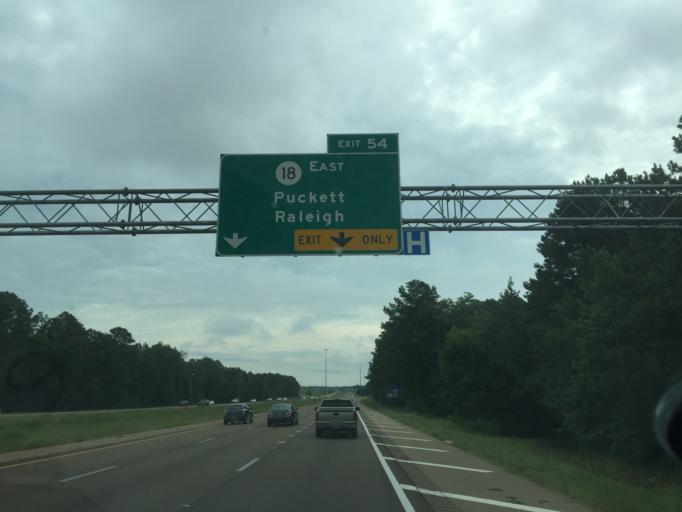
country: US
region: Mississippi
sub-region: Rankin County
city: Brandon
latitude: 32.2753
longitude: -90.0475
